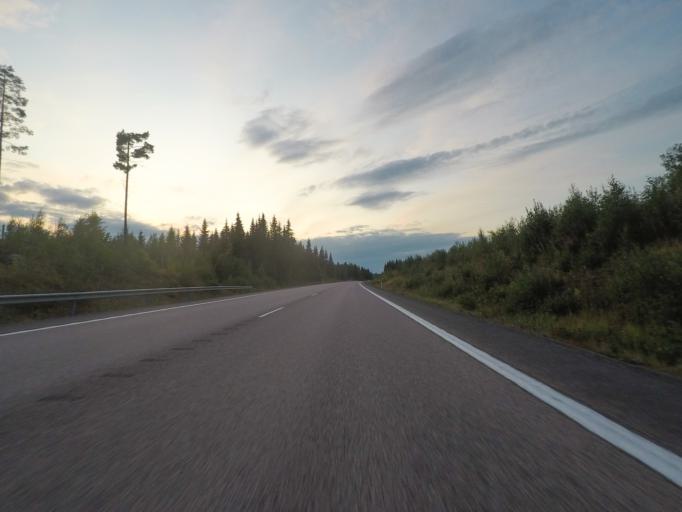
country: FI
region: Central Finland
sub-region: Jyvaeskylae
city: Saeynaetsalo
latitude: 62.1351
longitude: 25.9108
